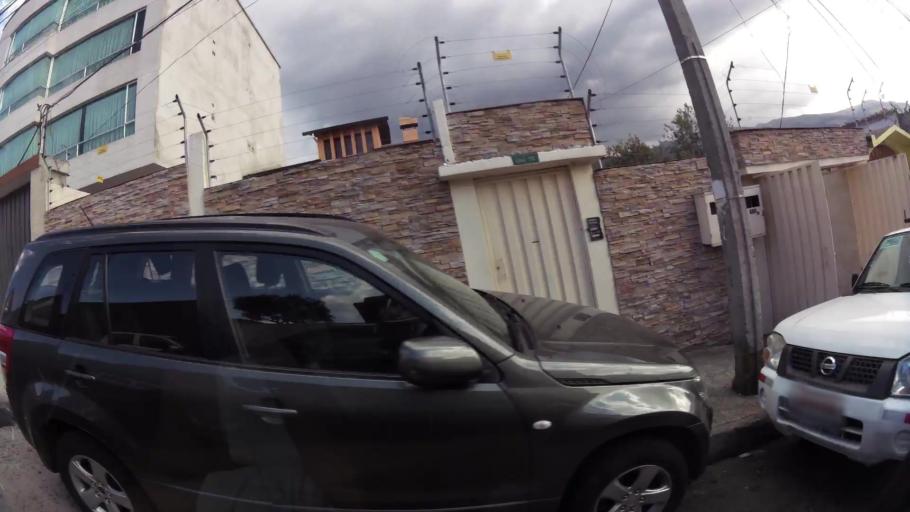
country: EC
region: Pichincha
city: Quito
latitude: -0.1219
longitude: -78.4861
